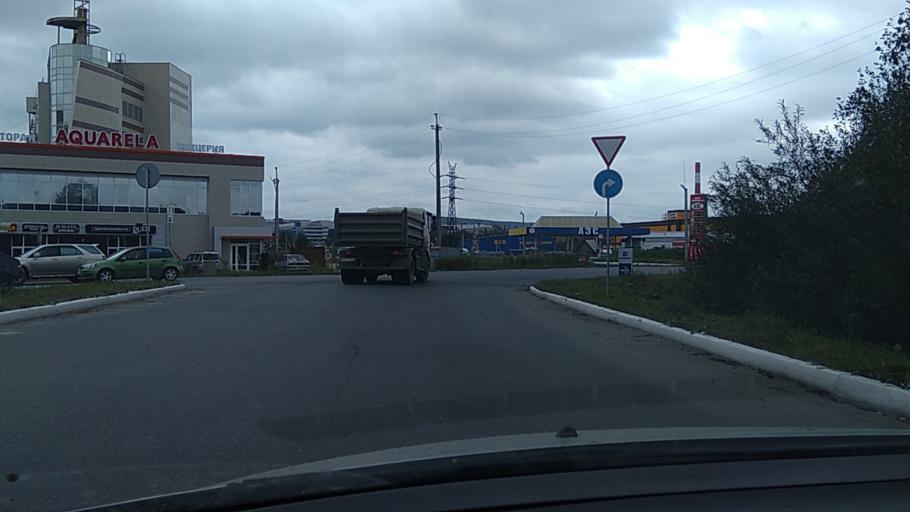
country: RU
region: Chelyabinsk
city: Zlatoust
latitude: 55.1185
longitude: 59.6986
